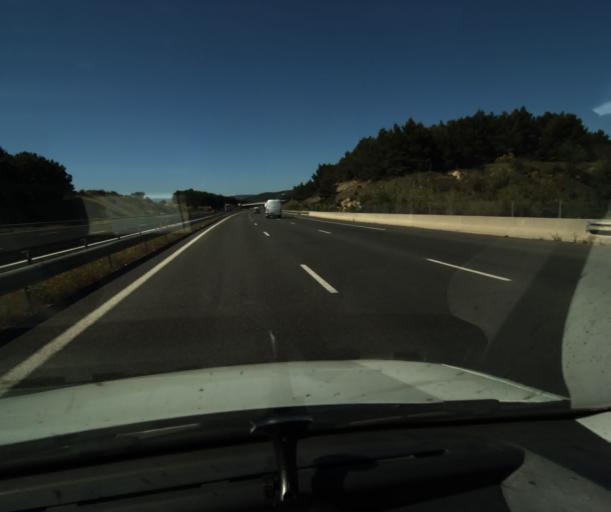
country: FR
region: Languedoc-Roussillon
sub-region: Departement de l'Aude
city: Peyriac-de-Mer
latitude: 43.1067
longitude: 2.9485
